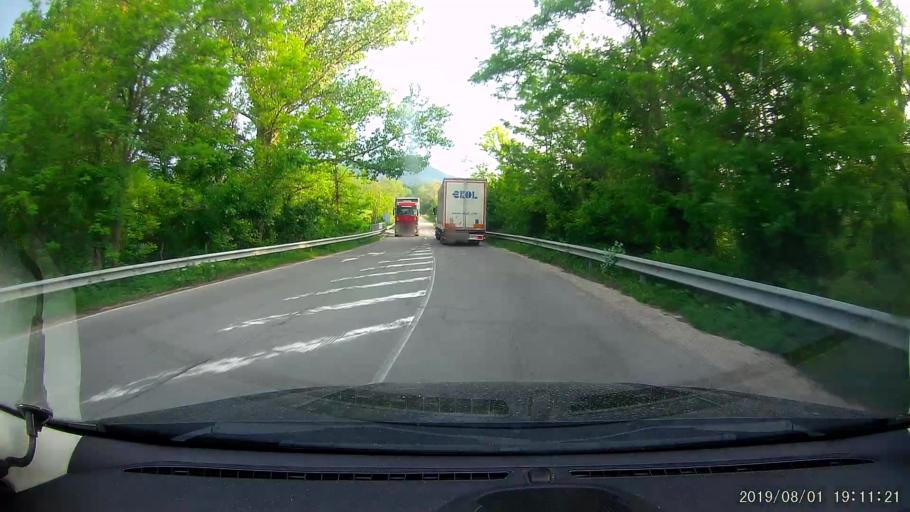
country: BG
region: Shumen
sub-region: Obshtina Smyadovo
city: Smyadovo
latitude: 42.9757
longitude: 26.9618
